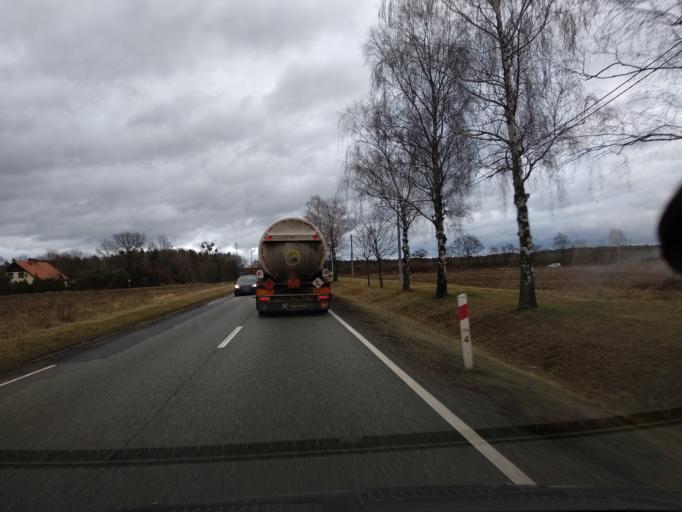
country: PL
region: Lower Silesian Voivodeship
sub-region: Powiat olesnicki
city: Twardogora
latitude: 51.2954
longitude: 17.5271
